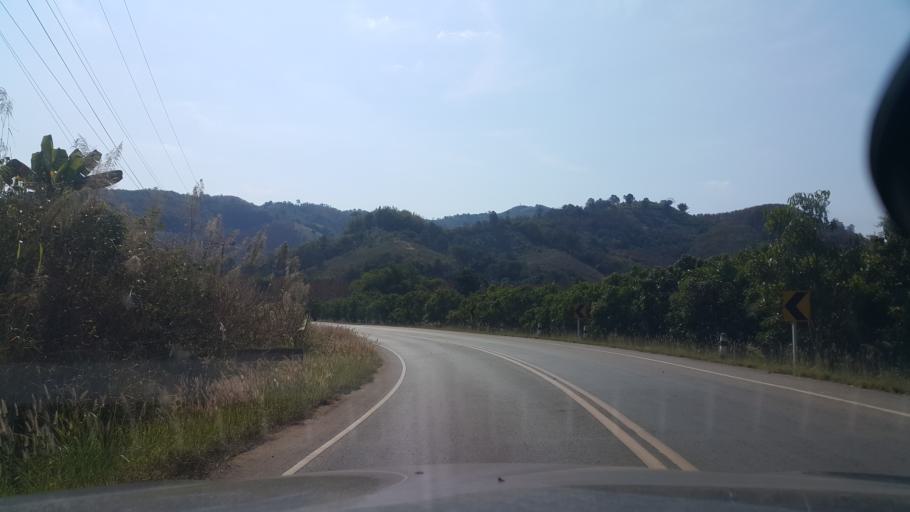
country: TH
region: Loei
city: Pak Chom
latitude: 18.1028
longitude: 102.0138
